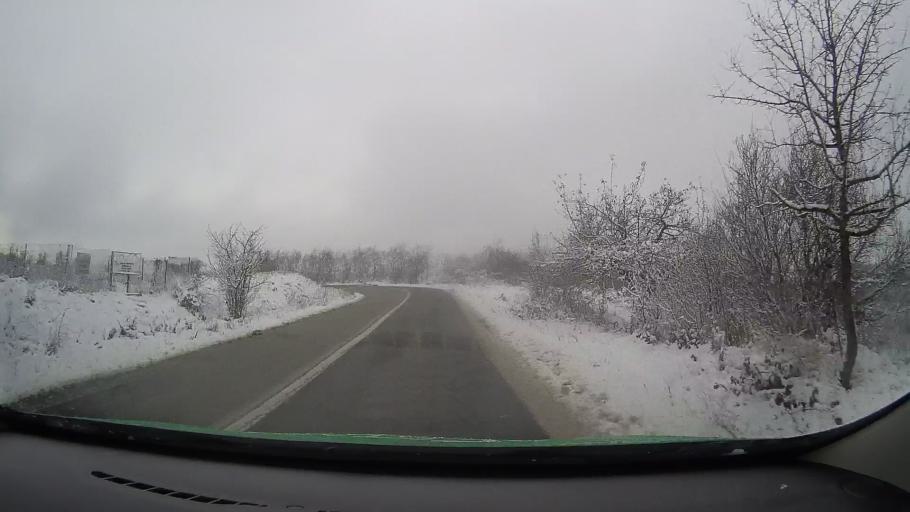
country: RO
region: Hunedoara
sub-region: Oras Hateg
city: Hateg
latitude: 45.6457
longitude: 22.9225
